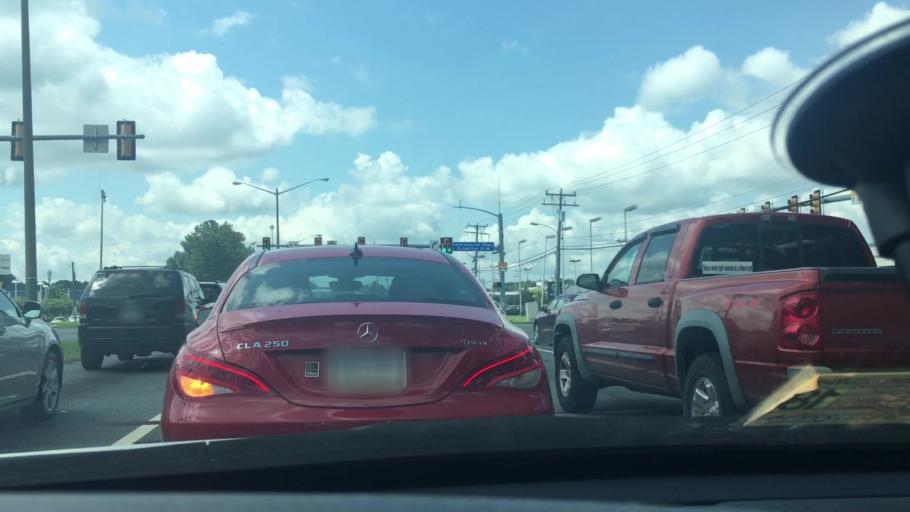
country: US
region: Virginia
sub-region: City of Chesapeake
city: Chesapeake
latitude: 36.7931
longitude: -76.2408
